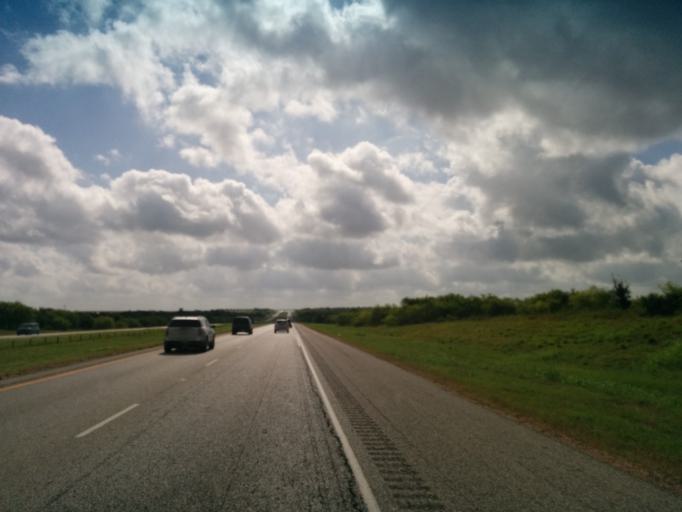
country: US
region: Texas
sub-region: Gonzales County
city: Waelder
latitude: 29.6648
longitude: -97.3540
